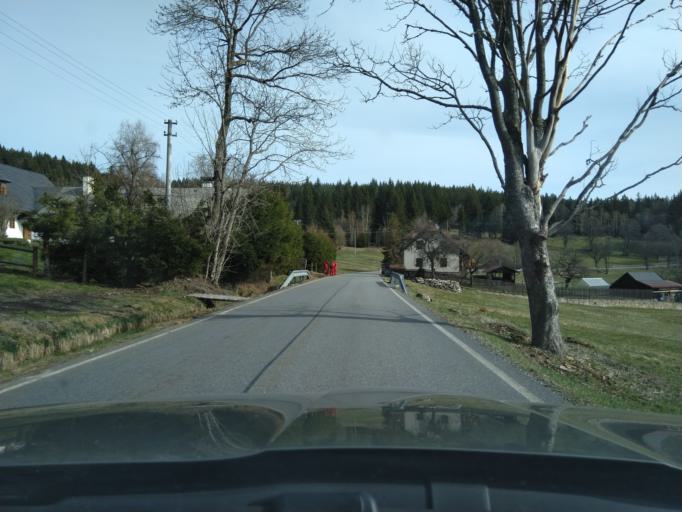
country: CZ
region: Jihocesky
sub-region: Okres Prachatice
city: Stachy
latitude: 49.0772
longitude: 13.6341
